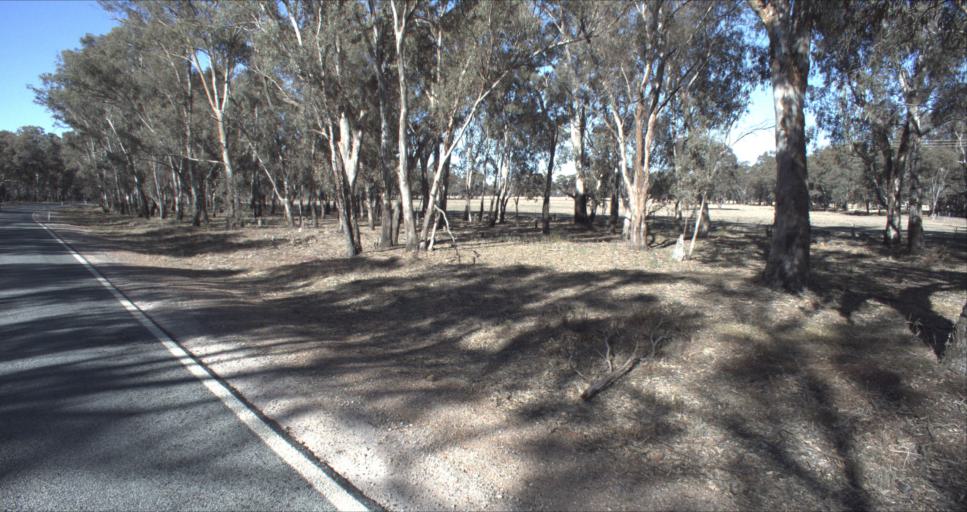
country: AU
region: New South Wales
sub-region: Leeton
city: Leeton
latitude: -34.6262
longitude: 146.3793
